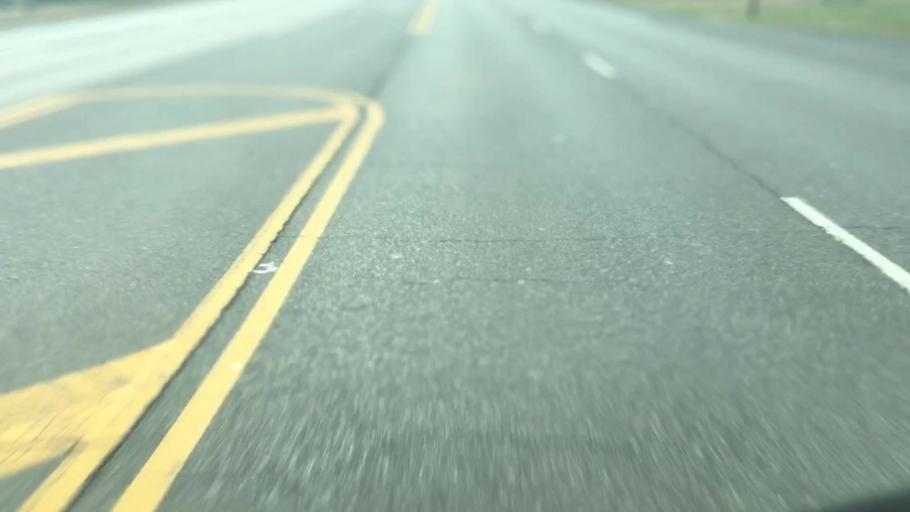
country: US
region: Alabama
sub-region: Walker County
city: Jasper
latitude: 33.8184
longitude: -87.2336
